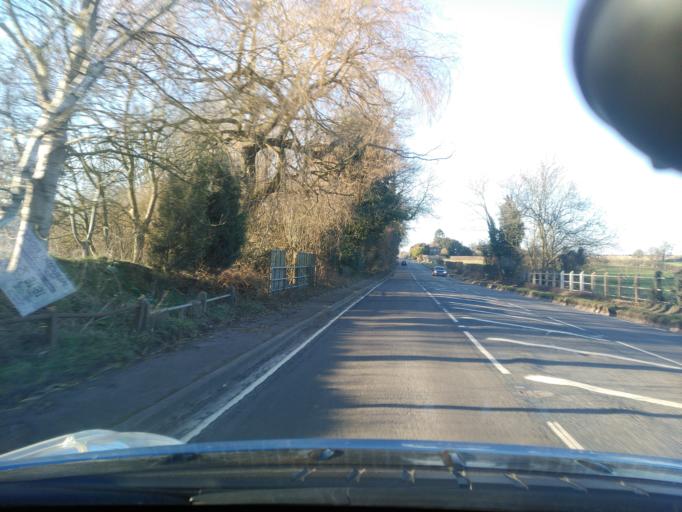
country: GB
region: England
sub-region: Hertfordshire
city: Redbourn
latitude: 51.7885
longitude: -0.3875
